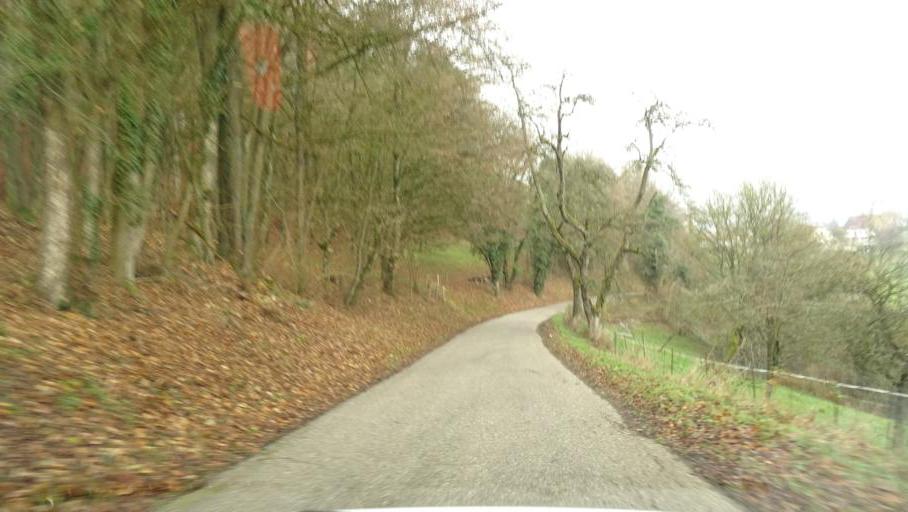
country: DE
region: Baden-Wuerttemberg
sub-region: Karlsruhe Region
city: Neckarzimmern
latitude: 49.3178
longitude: 9.1008
